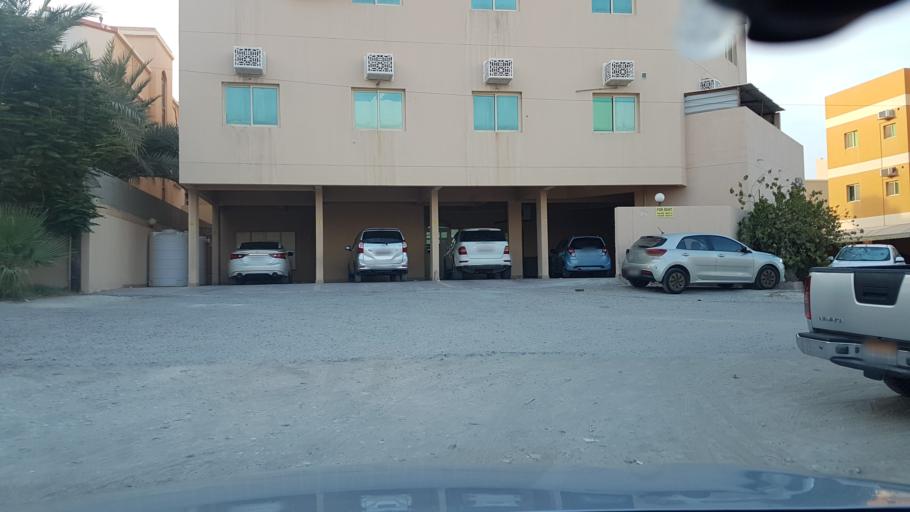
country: BH
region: Manama
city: Jidd Hafs
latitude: 26.2171
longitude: 50.4738
